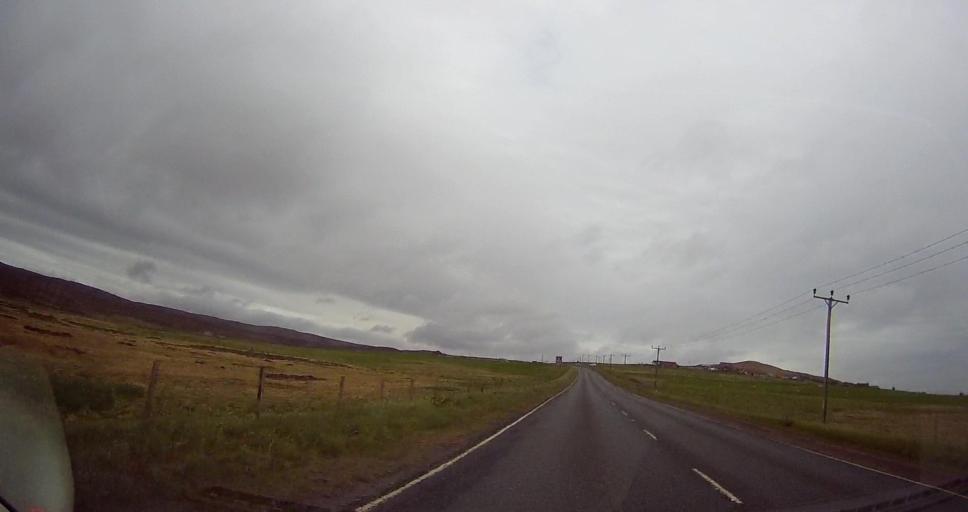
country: GB
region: Scotland
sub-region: Shetland Islands
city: Lerwick
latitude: 60.1940
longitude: -1.2321
